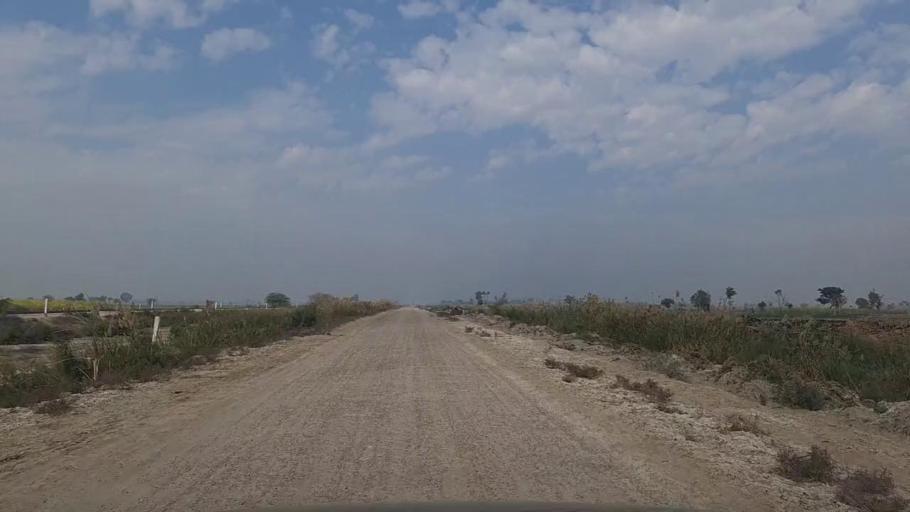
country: PK
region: Sindh
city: Daur
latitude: 26.3852
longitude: 68.3527
